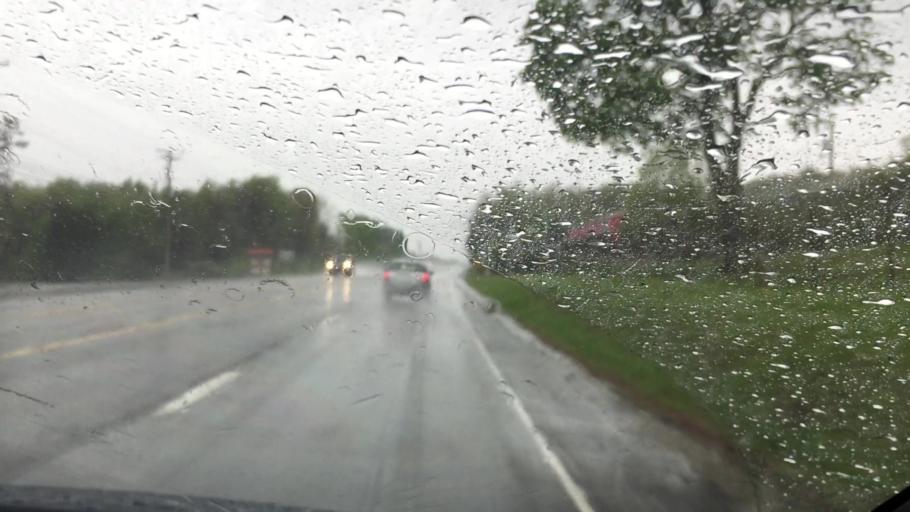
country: US
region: Pennsylvania
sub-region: Butler County
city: Nixon
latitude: 40.7467
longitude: -79.9253
